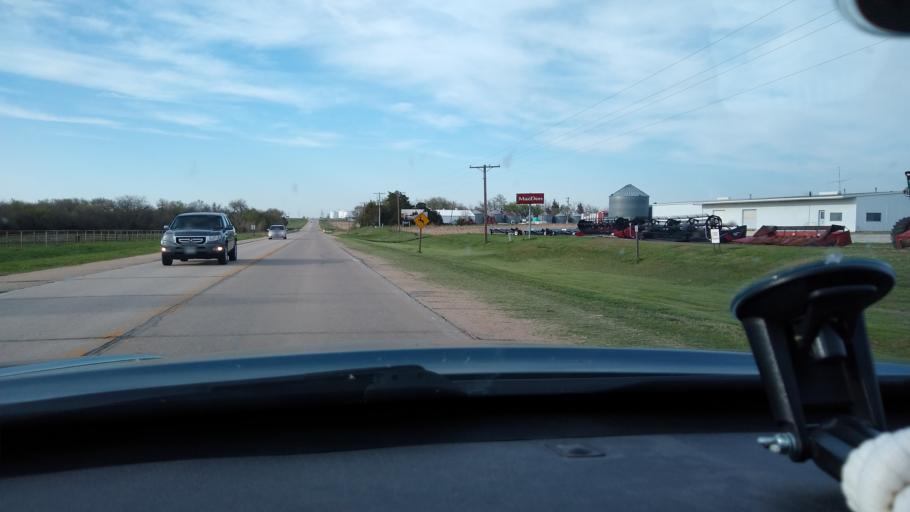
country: US
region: Nebraska
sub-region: Fillmore County
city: Geneva
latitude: 40.5406
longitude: -97.5958
